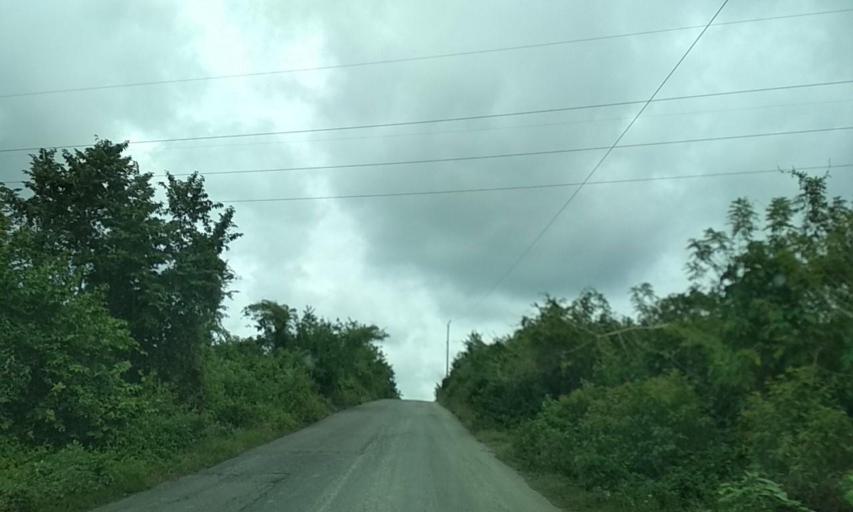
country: MX
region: Puebla
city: Espinal
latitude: 20.3283
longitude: -97.4124
